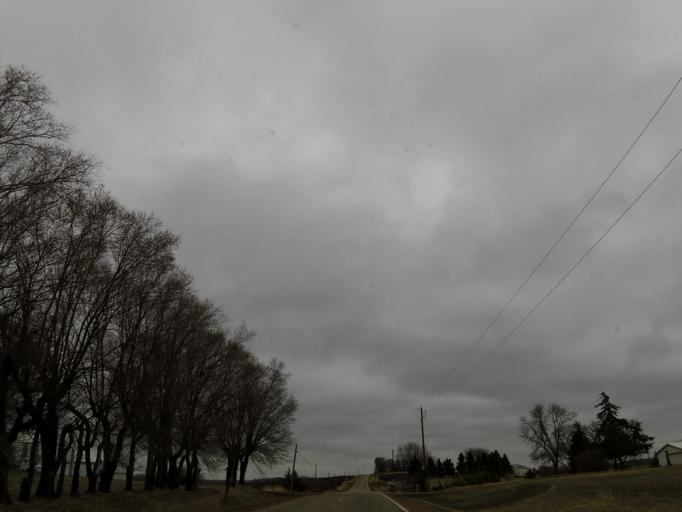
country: US
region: Minnesota
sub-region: Scott County
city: Shakopee
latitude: 44.7134
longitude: -93.5412
